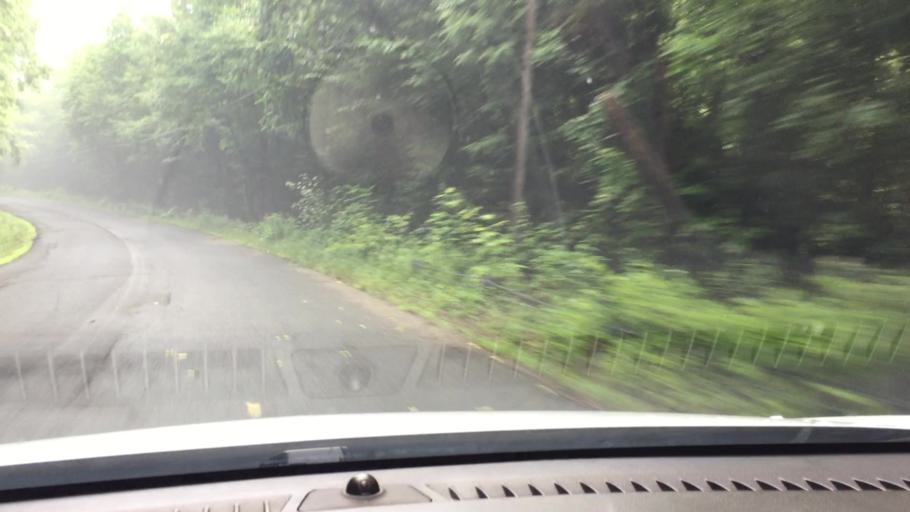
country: US
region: Massachusetts
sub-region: Hampshire County
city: Chesterfield
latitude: 42.2946
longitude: -72.9047
